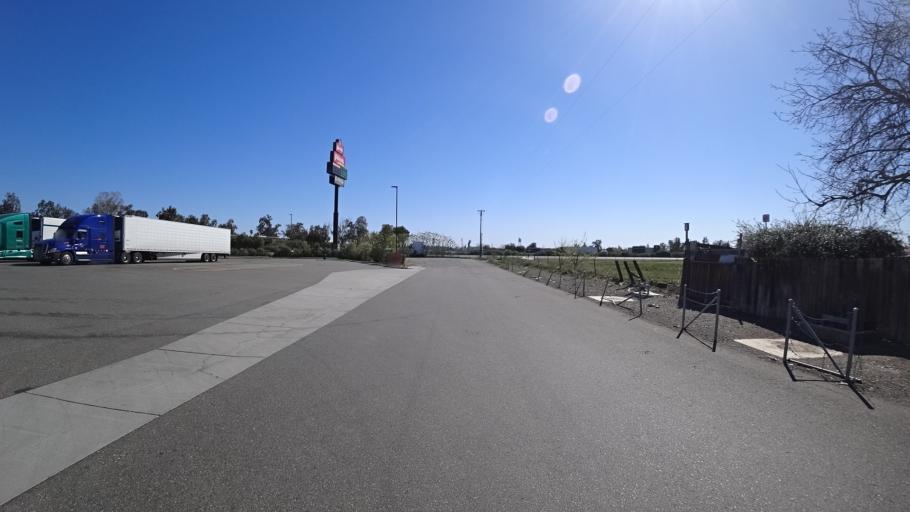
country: US
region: California
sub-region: Glenn County
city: Orland
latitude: 39.7497
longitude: -122.2072
